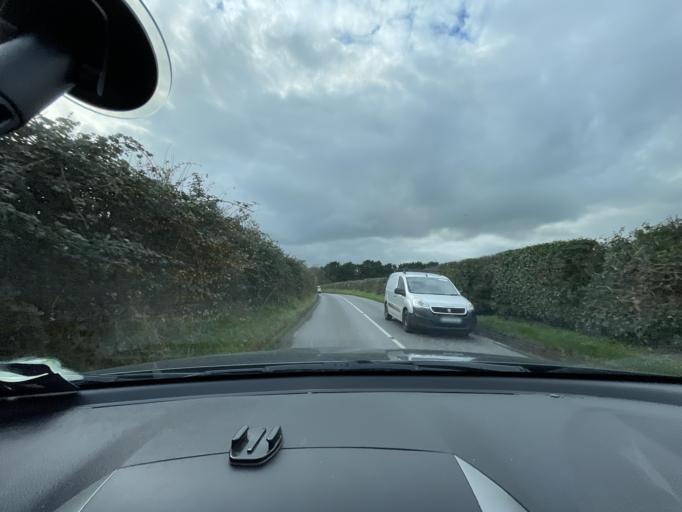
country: IE
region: Leinster
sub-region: Lu
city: Clogherhead
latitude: 53.7880
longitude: -6.2416
